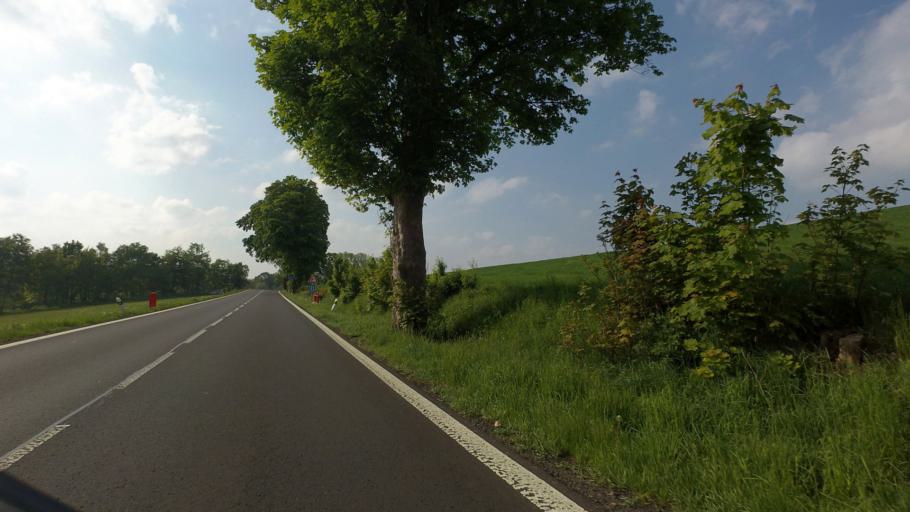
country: CZ
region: Ustecky
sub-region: Okres Decin
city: Sluknov
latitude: 50.9967
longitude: 14.4773
